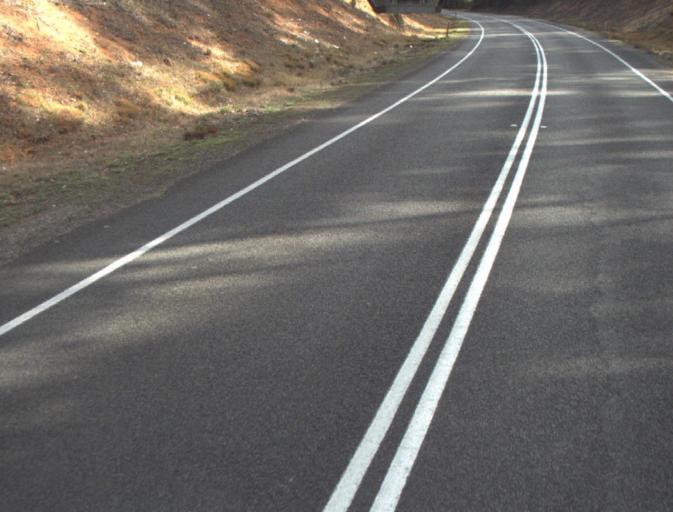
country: AU
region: Tasmania
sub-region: Launceston
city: Mayfield
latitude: -41.3082
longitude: 147.2037
